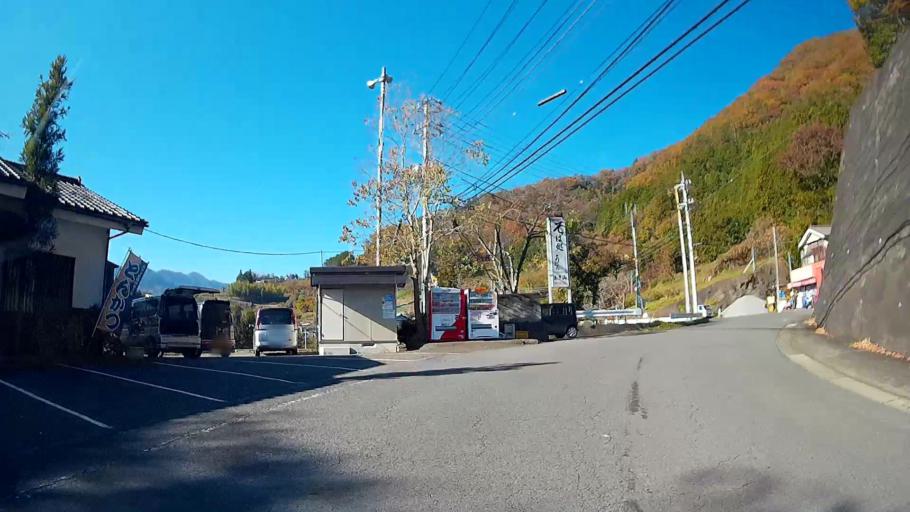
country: JP
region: Yamanashi
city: Uenohara
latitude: 35.5807
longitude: 139.1061
